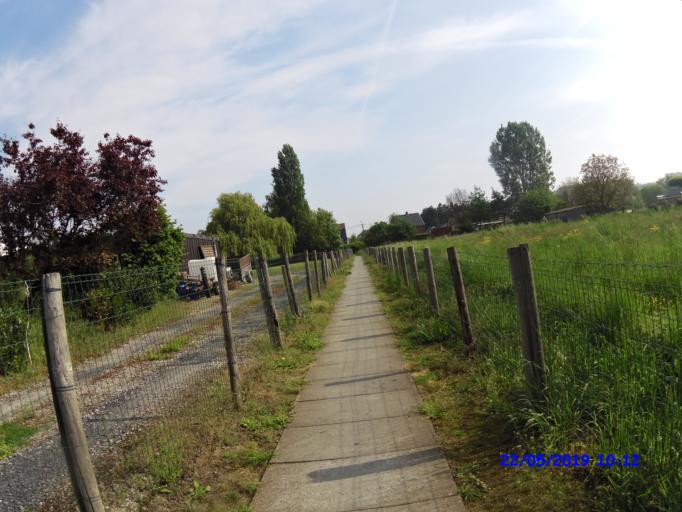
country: BE
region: Flanders
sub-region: Provincie Oost-Vlaanderen
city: Oudenaarde
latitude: 50.8269
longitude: 3.5996
